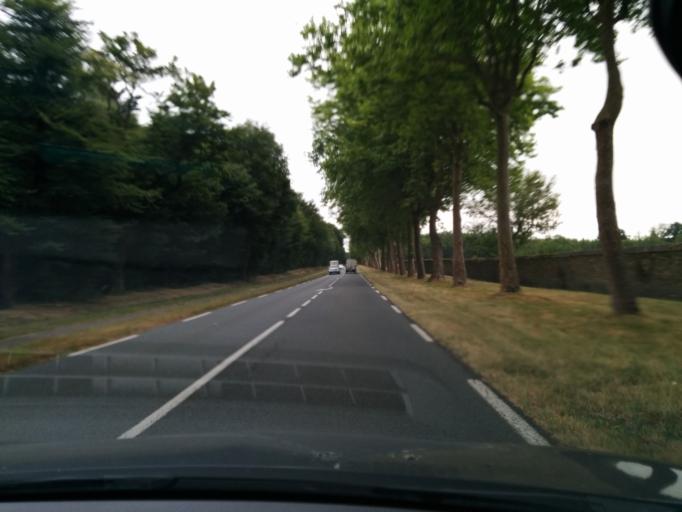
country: FR
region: Ile-de-France
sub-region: Departement des Yvelines
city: Rambouillet
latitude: 48.6644
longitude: 1.8085
